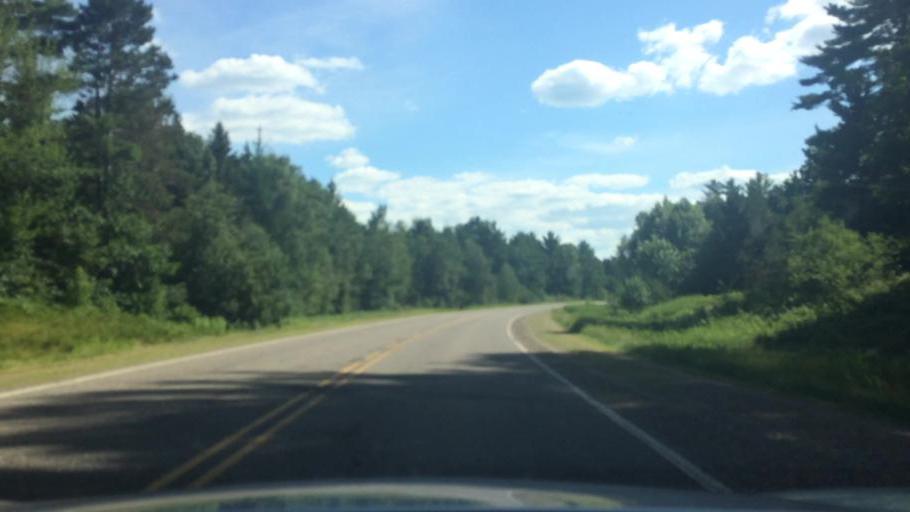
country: US
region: Wisconsin
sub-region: Vilas County
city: Lac du Flambeau
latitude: 46.0640
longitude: -89.6453
